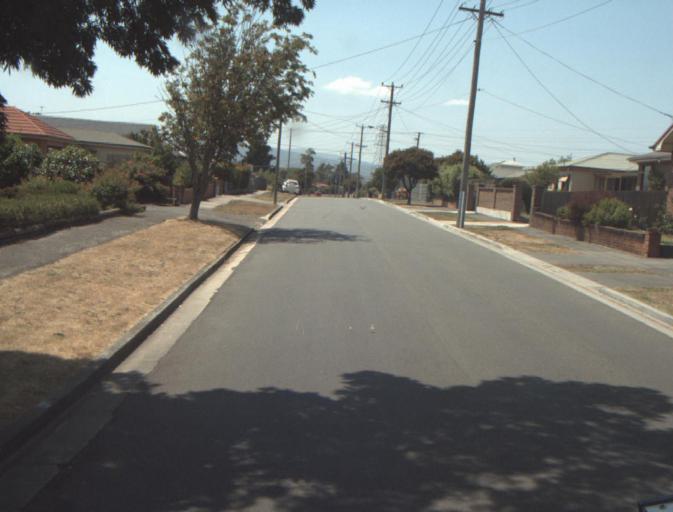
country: AU
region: Tasmania
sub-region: Launceston
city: Summerhill
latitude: -41.4852
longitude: 147.1679
